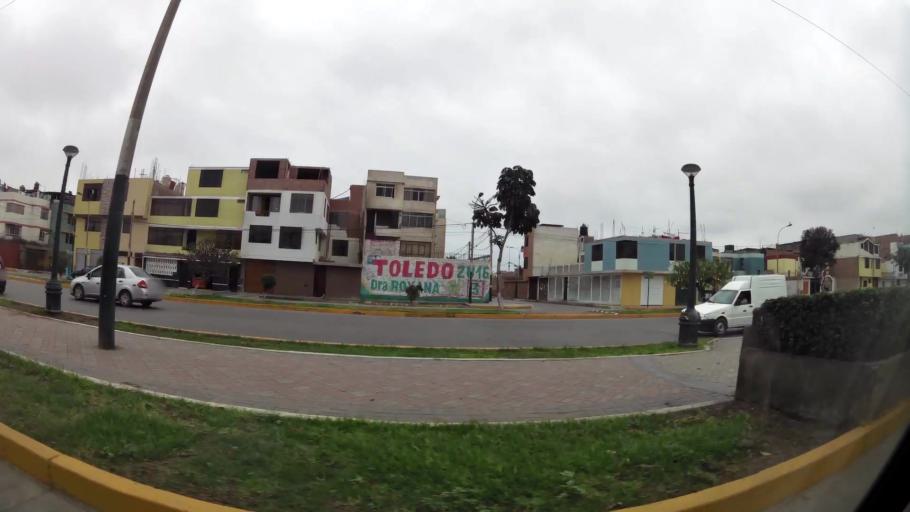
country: PE
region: Callao
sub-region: Callao
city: Callao
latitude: -12.0601
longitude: -77.1153
